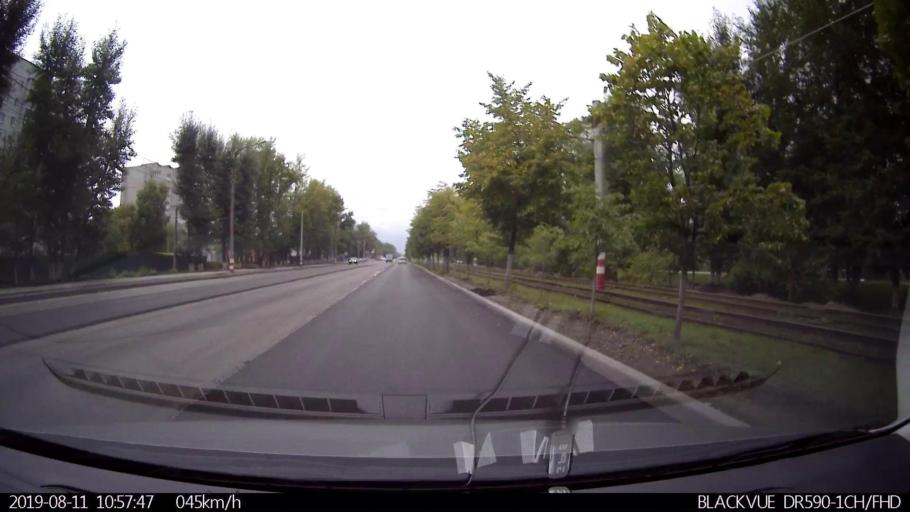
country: RU
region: Ulyanovsk
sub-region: Ulyanovskiy Rayon
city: Ulyanovsk
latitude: 54.2566
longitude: 48.3204
